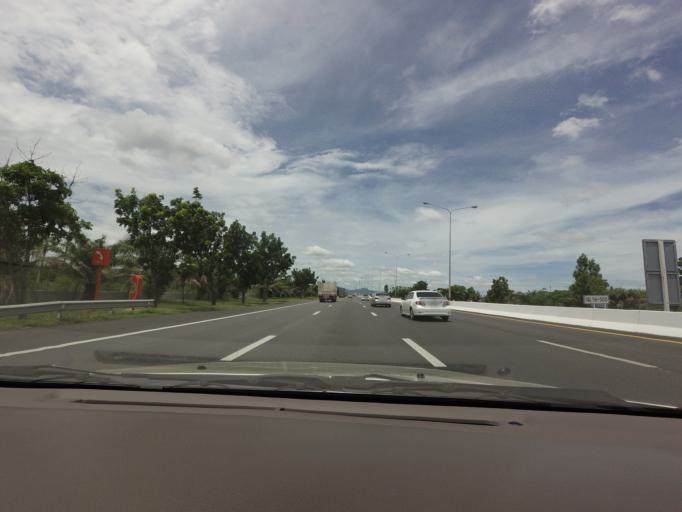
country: TH
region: Chon Buri
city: Phan Thong
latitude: 13.4874
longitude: 101.0468
